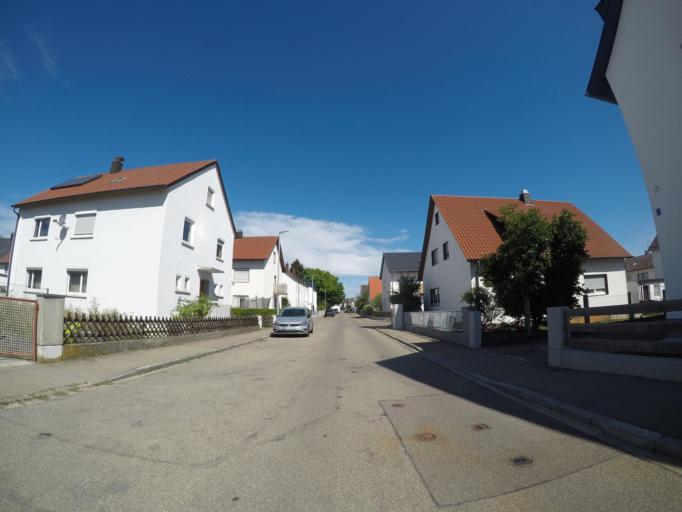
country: DE
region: Bavaria
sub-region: Swabia
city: Senden
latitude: 48.3441
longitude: 10.0375
